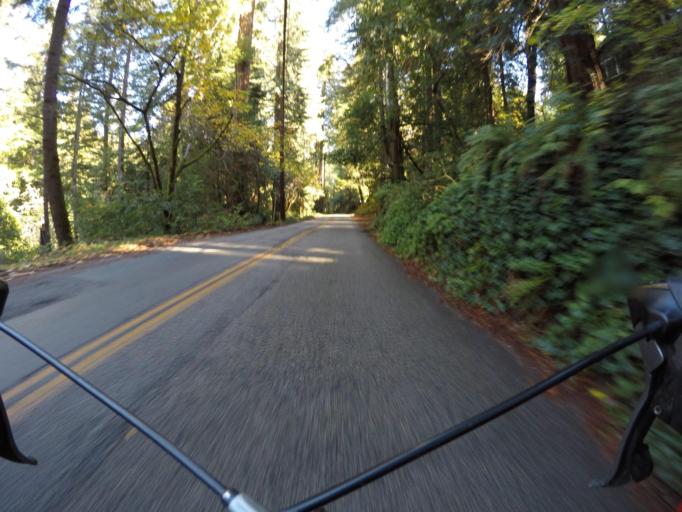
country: US
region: California
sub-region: Santa Cruz County
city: Scotts Valley
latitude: 37.0967
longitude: -121.9940
